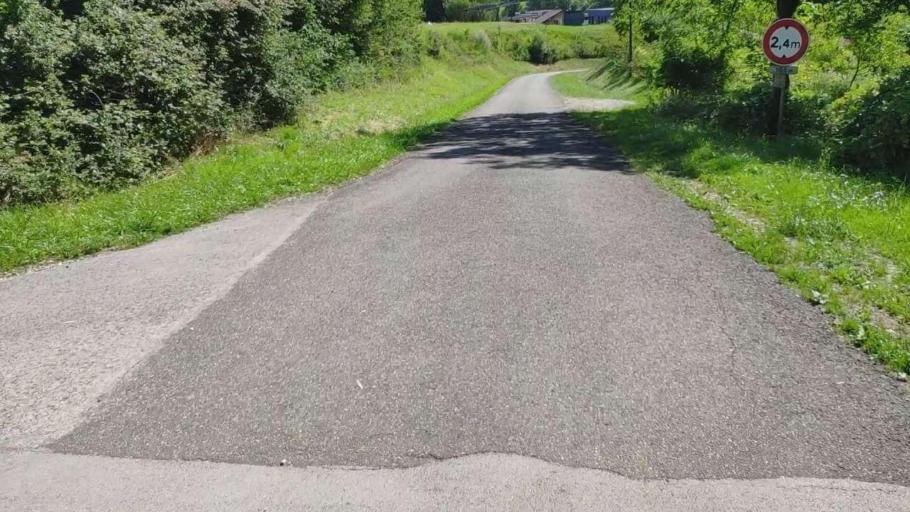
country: FR
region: Franche-Comte
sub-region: Departement du Jura
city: Poligny
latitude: 46.8061
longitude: 5.5777
